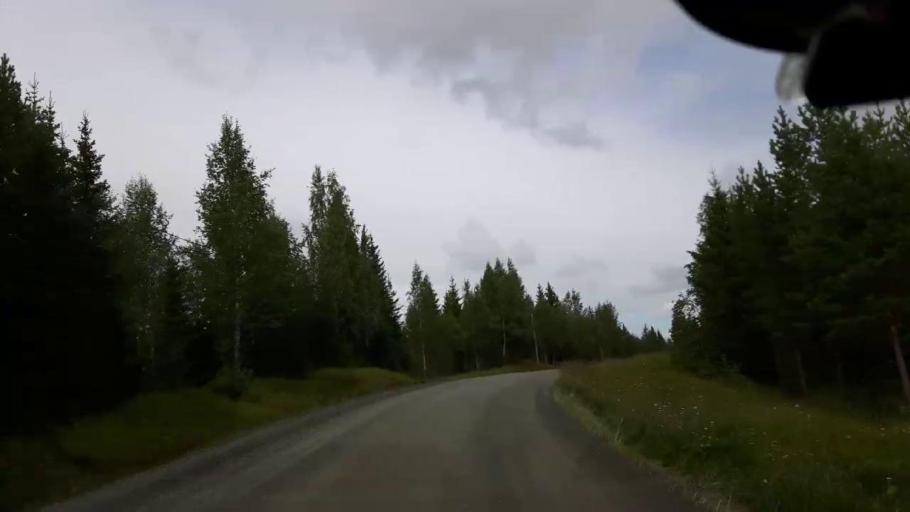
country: SE
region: Jaemtland
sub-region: Krokoms Kommun
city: Valla
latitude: 63.4171
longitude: 14.0812
